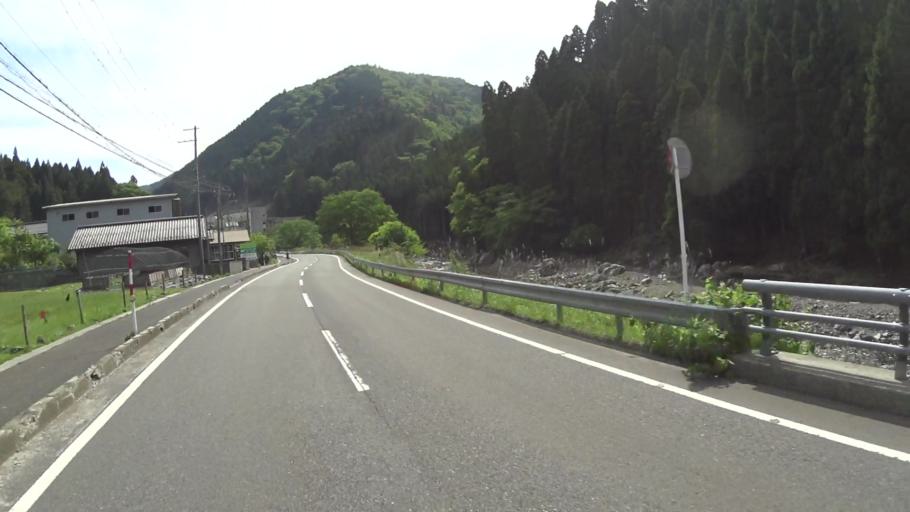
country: JP
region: Shiga Prefecture
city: Kitahama
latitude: 35.2369
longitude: 135.8643
